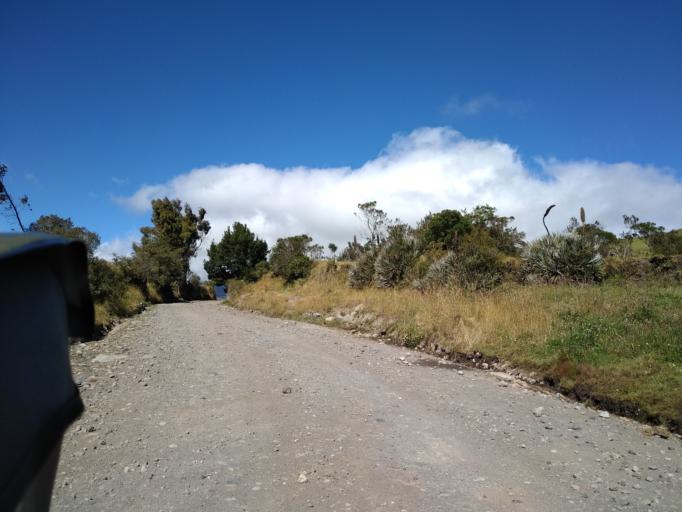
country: EC
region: Pichincha
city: Machachi
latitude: -0.5337
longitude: -78.4814
